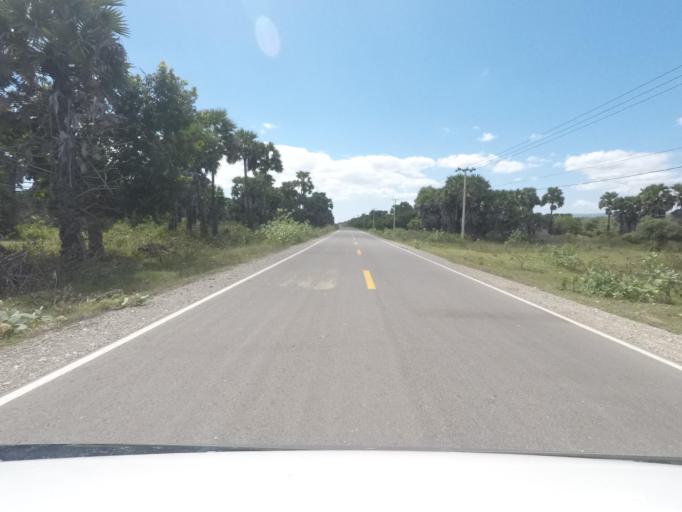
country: TL
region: Lautem
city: Lospalos
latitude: -8.3899
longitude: 126.8502
